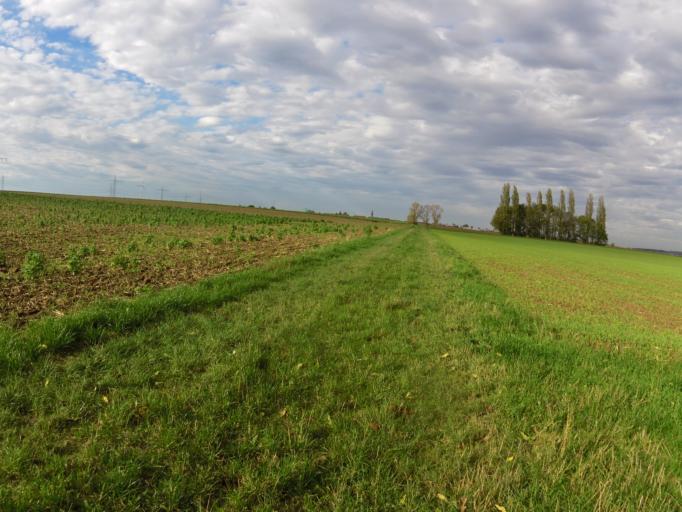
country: DE
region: Bavaria
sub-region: Regierungsbezirk Unterfranken
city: Biebelried
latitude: 49.7322
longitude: 10.0695
